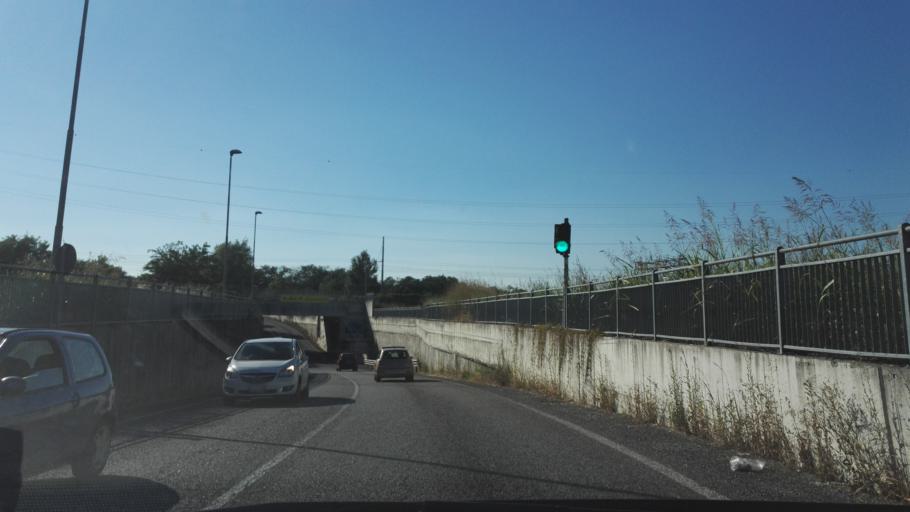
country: IT
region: Lombardy
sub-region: Citta metropolitana di Milano
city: Locate di Triulzi
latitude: 45.3647
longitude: 9.2275
